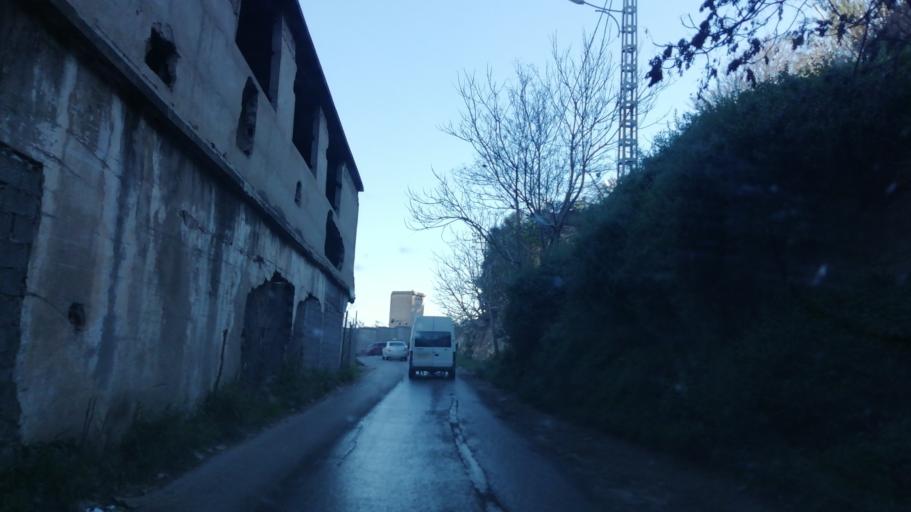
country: DZ
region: Oran
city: Oran
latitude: 35.6921
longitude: -0.6617
